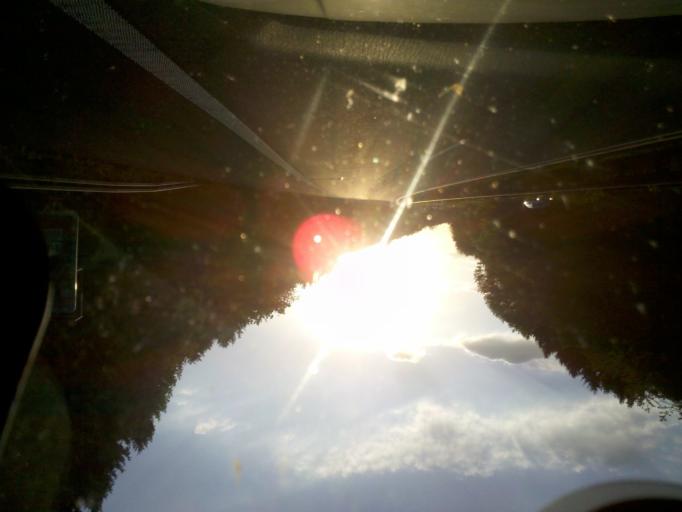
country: DE
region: North Rhine-Westphalia
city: Bergneustadt
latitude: 50.9808
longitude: 7.6348
